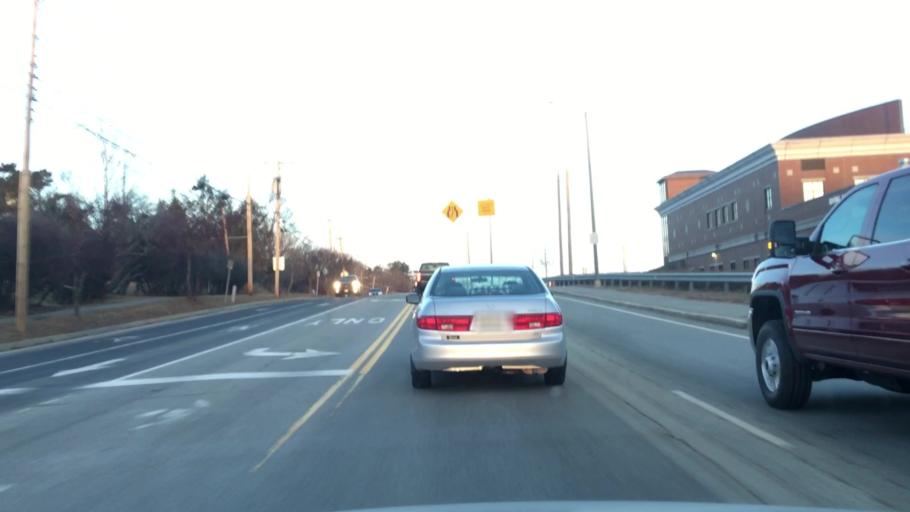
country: US
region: Maine
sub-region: Penobscot County
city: Brewer
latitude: 44.8084
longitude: -68.7534
